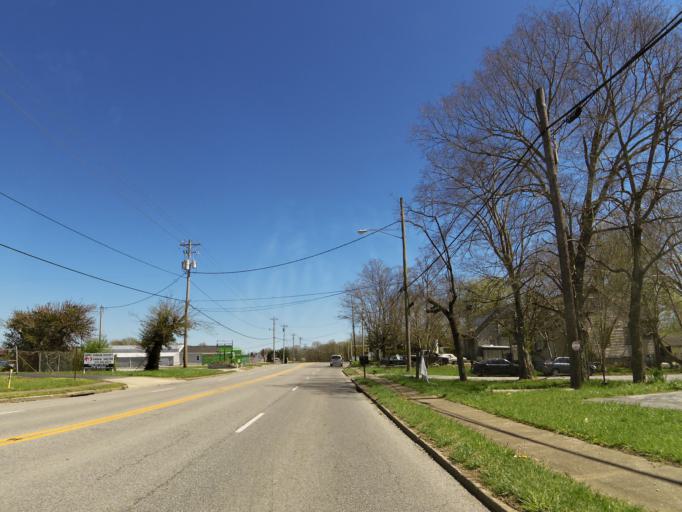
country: US
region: Kentucky
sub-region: Warren County
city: Bowling Green
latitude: 37.0059
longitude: -86.4163
